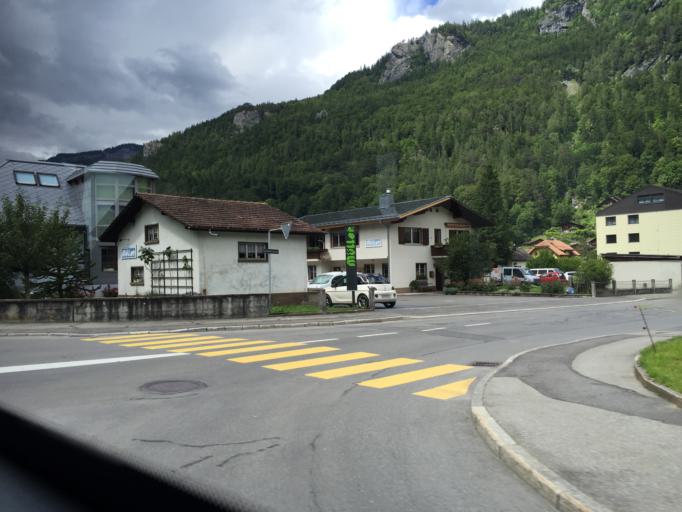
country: CH
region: Bern
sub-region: Interlaken-Oberhasli District
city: Meiringen
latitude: 46.7295
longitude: 8.1812
